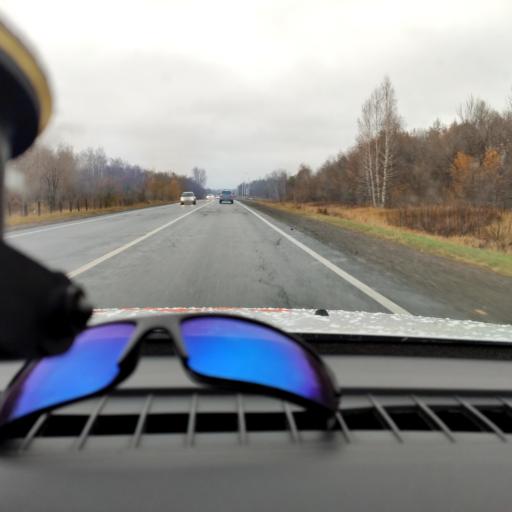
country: RU
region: Samara
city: Chapayevsk
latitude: 52.9947
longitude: 49.8138
